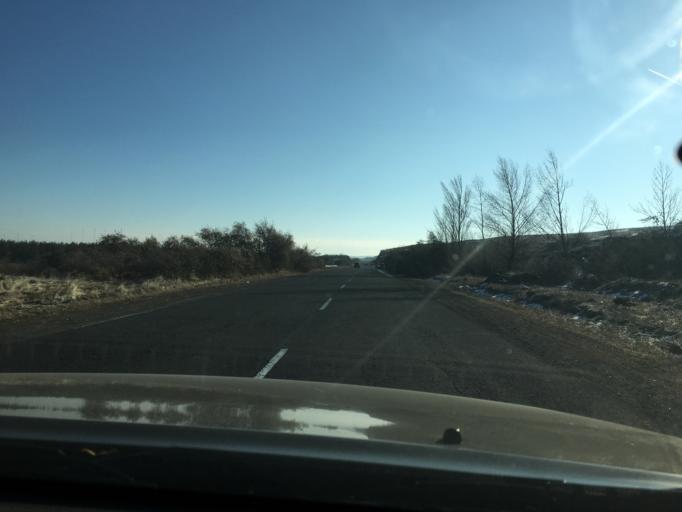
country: AM
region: Geghark'unik'i Marz
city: Gavarr
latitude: 40.4052
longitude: 45.1268
